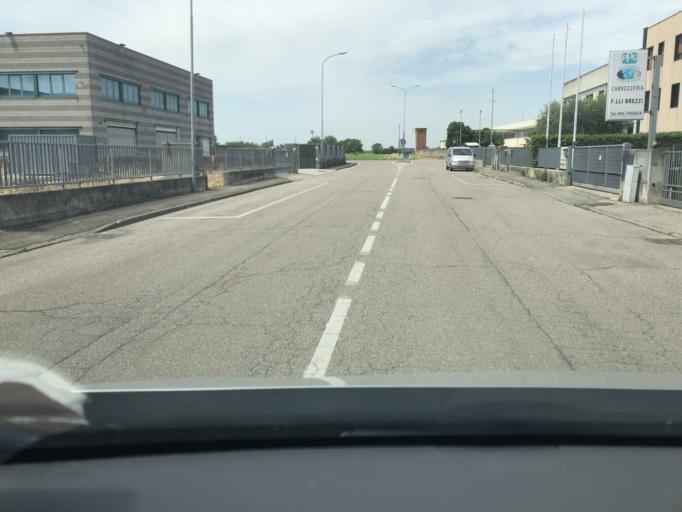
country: IT
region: Veneto
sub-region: Provincia di Verona
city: Valeggio sul Mincio
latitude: 45.3403
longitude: 10.7351
